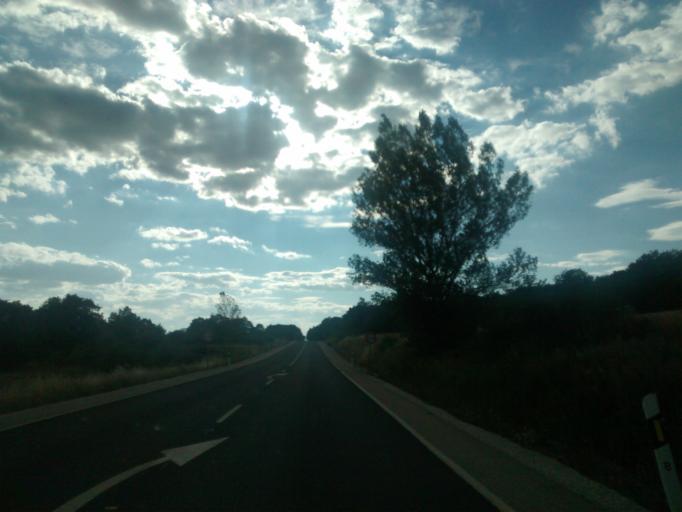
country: ES
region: Castille and Leon
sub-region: Provincia de Burgos
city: Basconcillos del Tozo
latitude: 42.6820
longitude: -3.9521
